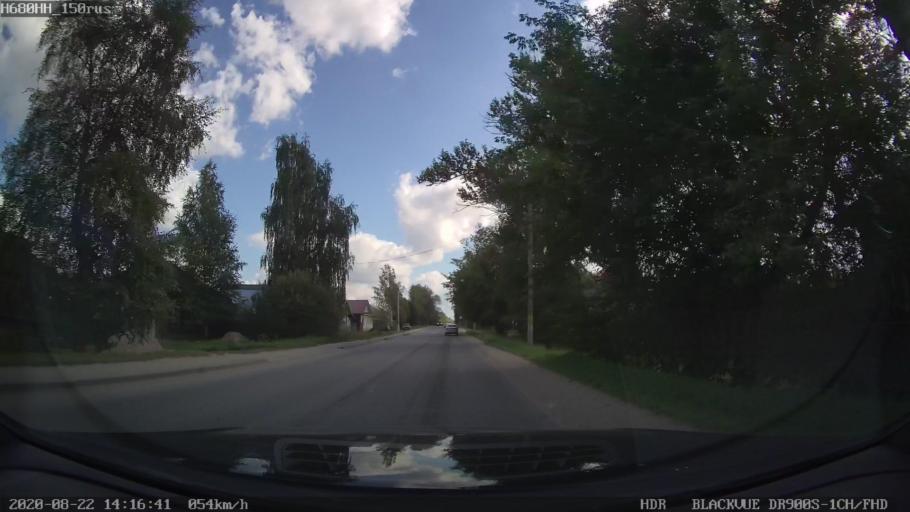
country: RU
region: Tverskaya
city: Bezhetsk
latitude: 57.7746
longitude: 36.6991
